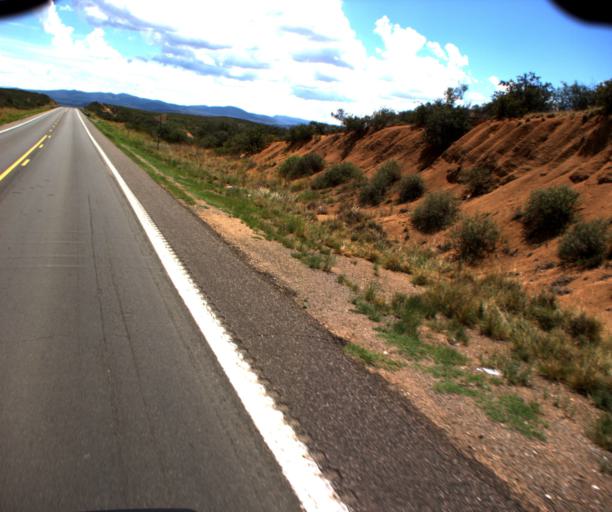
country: US
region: Arizona
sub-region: Yavapai County
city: Dewey-Humboldt
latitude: 34.5352
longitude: -112.1385
